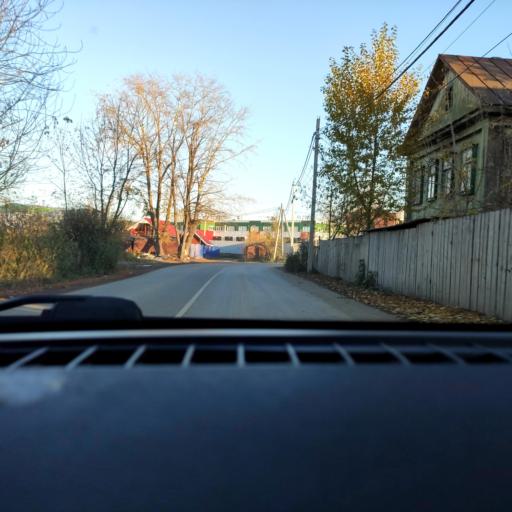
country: RU
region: Perm
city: Kondratovo
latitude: 58.0046
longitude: 56.1405
